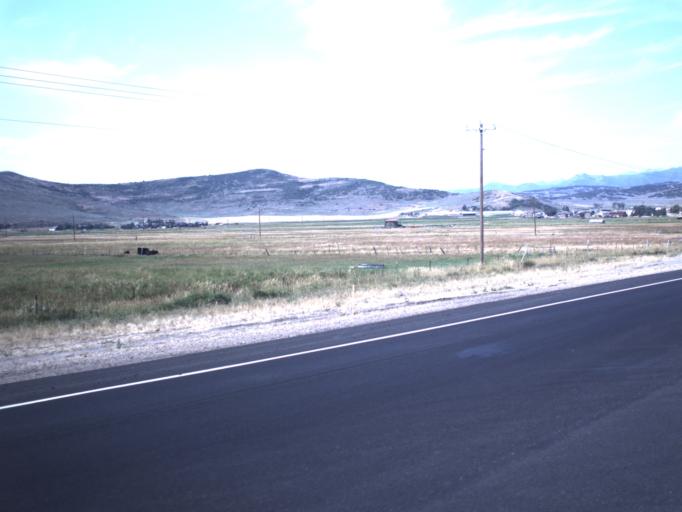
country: US
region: Utah
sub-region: Summit County
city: Kamas
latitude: 40.6400
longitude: -111.2972
